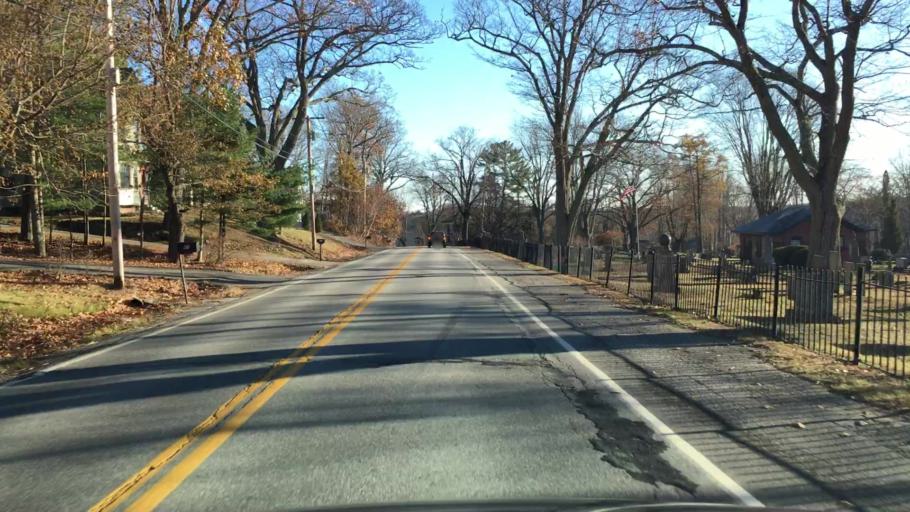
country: US
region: Maine
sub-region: Knox County
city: Camden
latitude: 44.2180
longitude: -69.0730
